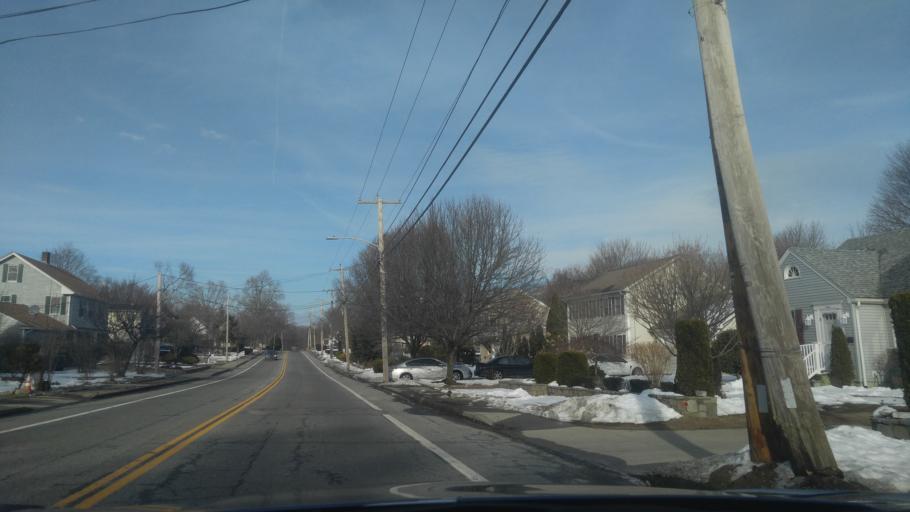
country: US
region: Rhode Island
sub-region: Kent County
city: West Warwick
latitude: 41.7323
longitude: -71.4856
